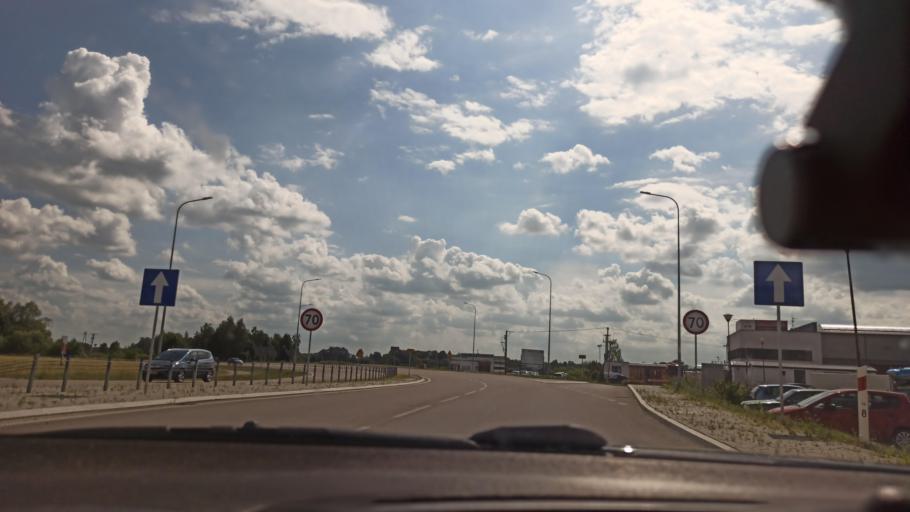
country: PL
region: Podlasie
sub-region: Powiat bialostocki
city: Turosn Koscielna
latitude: 53.0558
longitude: 23.0426
